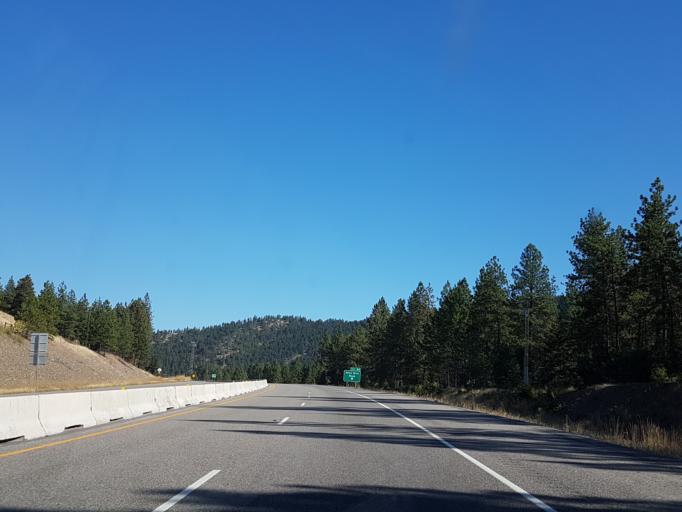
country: US
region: Montana
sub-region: Missoula County
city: Frenchtown
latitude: 47.0193
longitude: -114.3755
